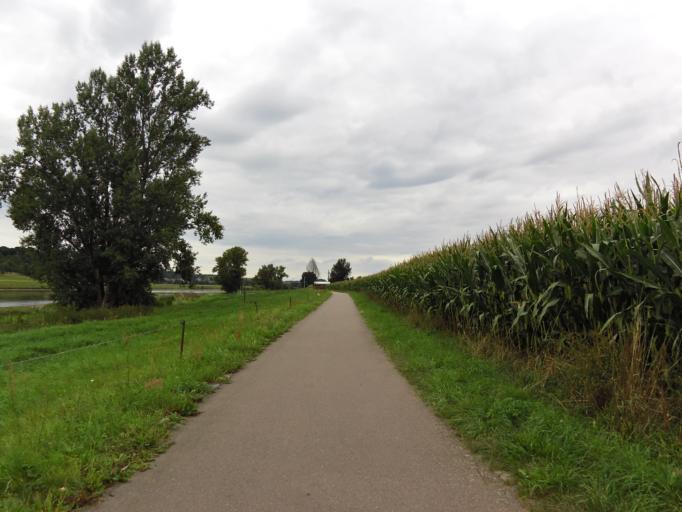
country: DE
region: Saxony
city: Meissen
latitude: 51.2076
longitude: 13.4074
